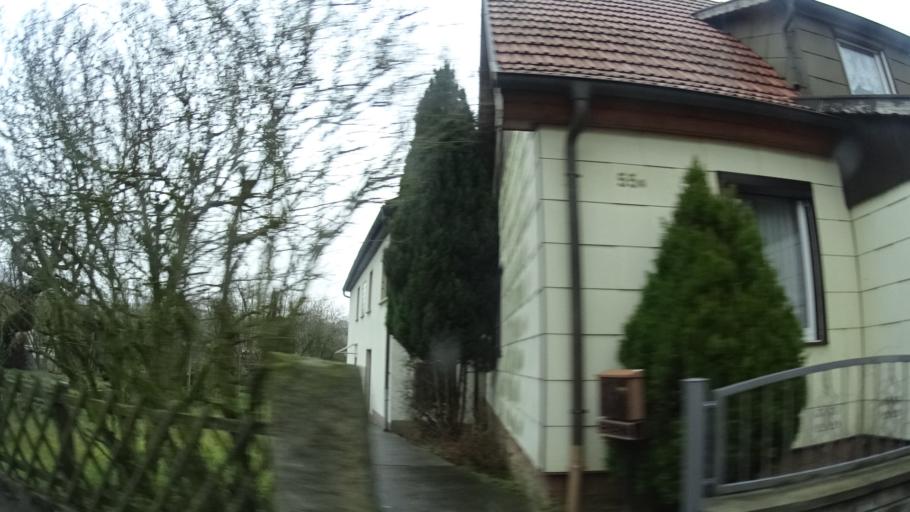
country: DE
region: Thuringia
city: Wolfershausen
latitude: 50.4665
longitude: 10.4379
